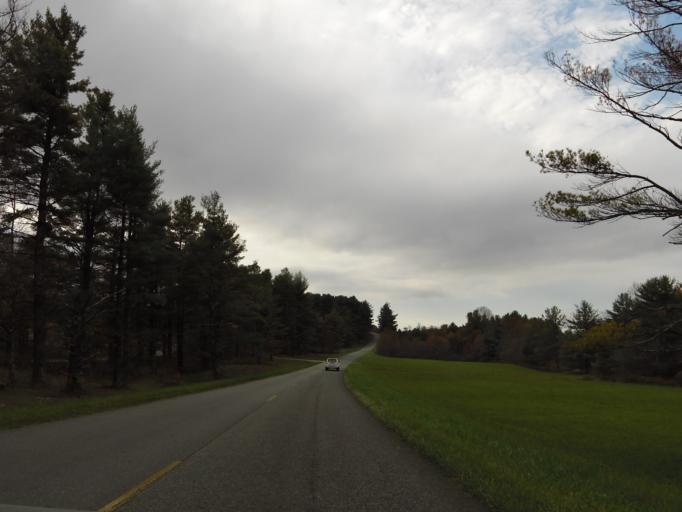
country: US
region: Virginia
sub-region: Carroll County
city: Cana
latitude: 36.6071
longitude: -80.7866
